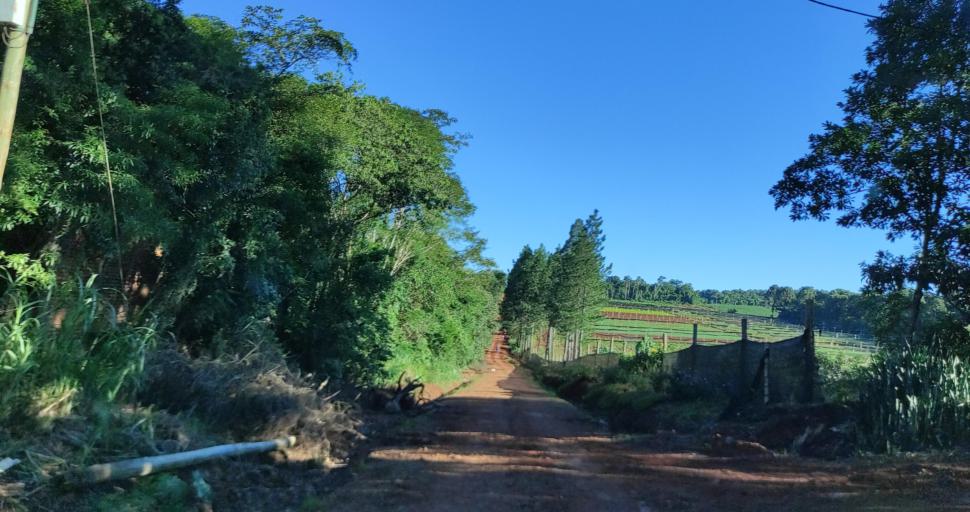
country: AR
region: Misiones
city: Puerto Rico
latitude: -26.8268
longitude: -55.0113
